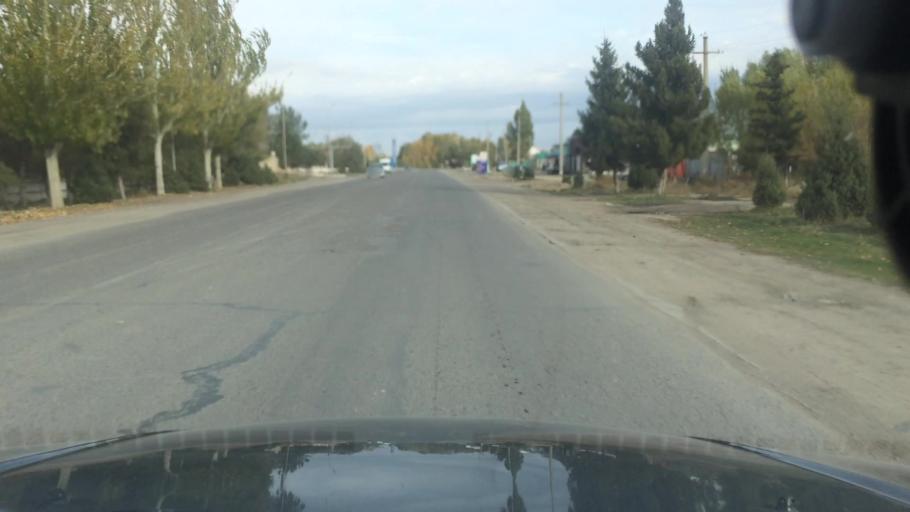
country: KG
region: Ysyk-Koel
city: Karakol
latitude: 42.5295
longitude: 78.3832
